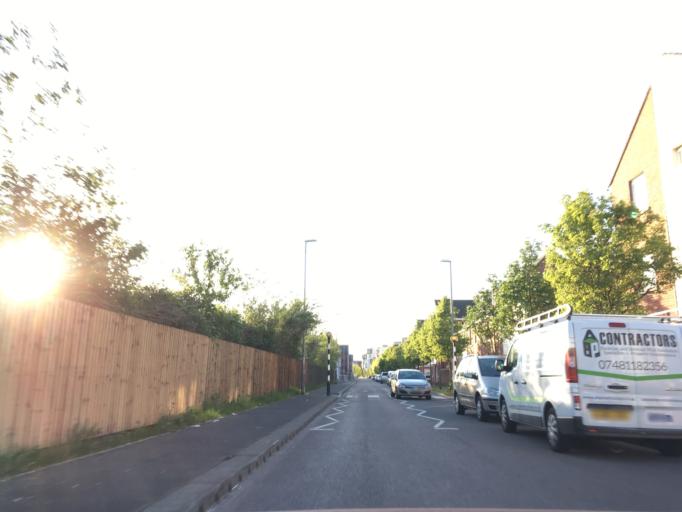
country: GB
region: Wales
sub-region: Newport
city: Newport
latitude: 51.5777
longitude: -2.9798
